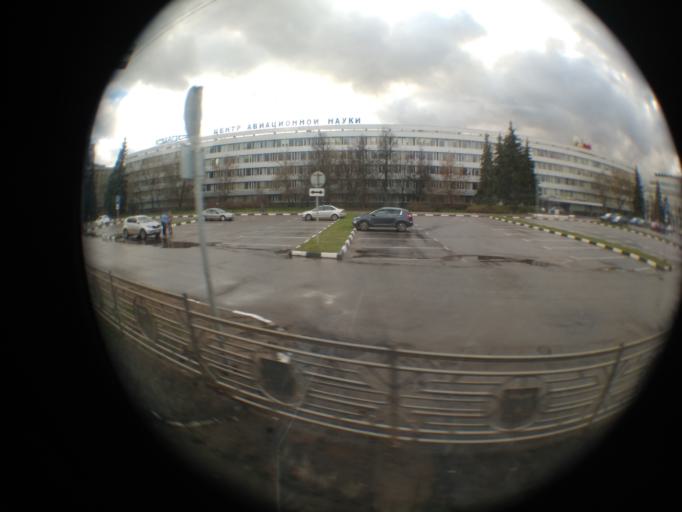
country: RU
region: Moskovskaya
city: Zhukovskiy
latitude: 55.5962
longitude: 38.1133
